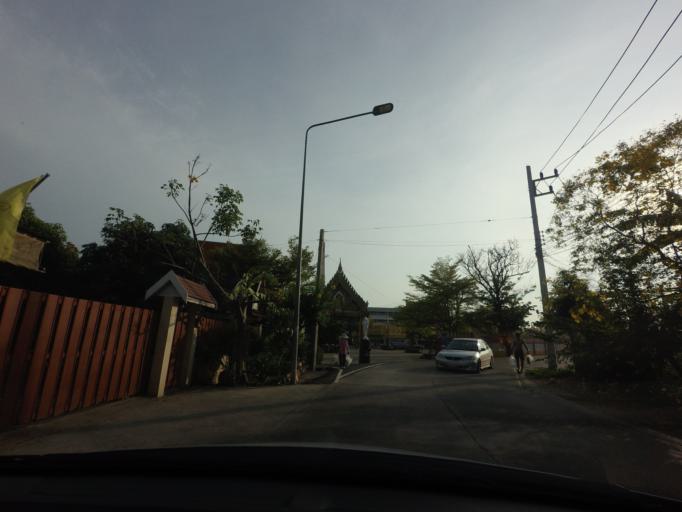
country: TH
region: Pathum Thani
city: Pathum Thani
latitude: 14.0373
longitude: 100.5469
